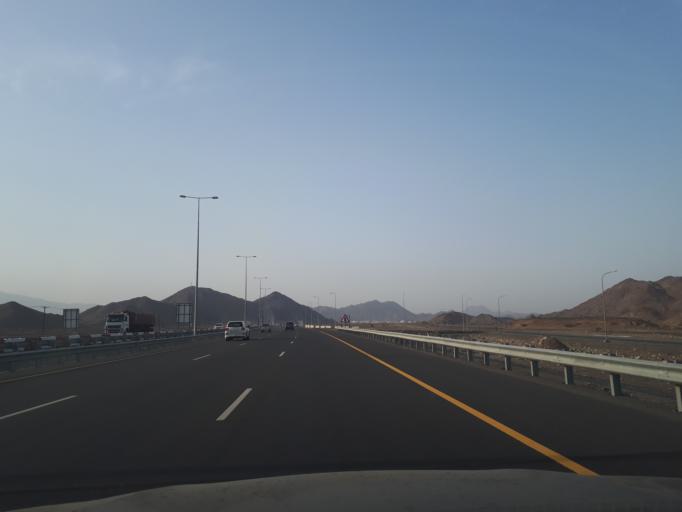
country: OM
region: Muhafazat ad Dakhiliyah
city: Sufalat Sama'il
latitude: 23.2946
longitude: 58.1104
